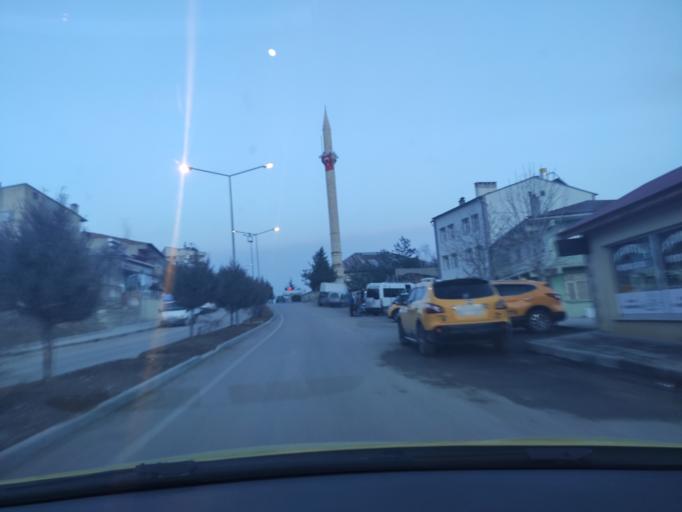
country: TR
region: Bayburt
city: Aydintepe
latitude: 40.3886
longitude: 40.1494
